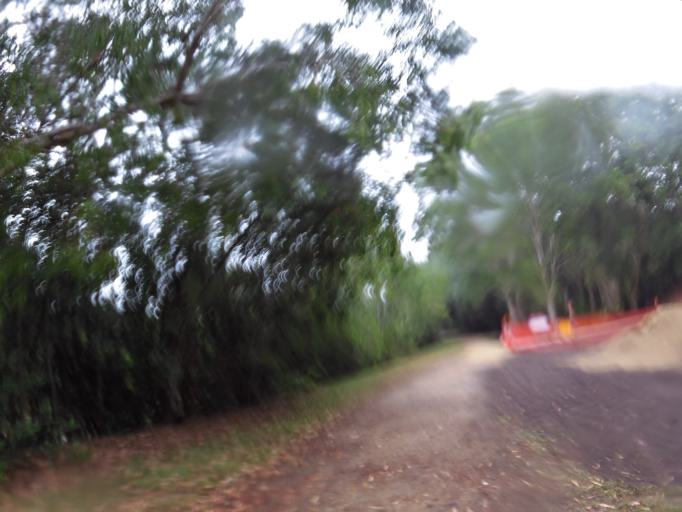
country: AU
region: Queensland
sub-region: Cairns
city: Cairns
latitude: -16.9010
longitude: 145.7516
